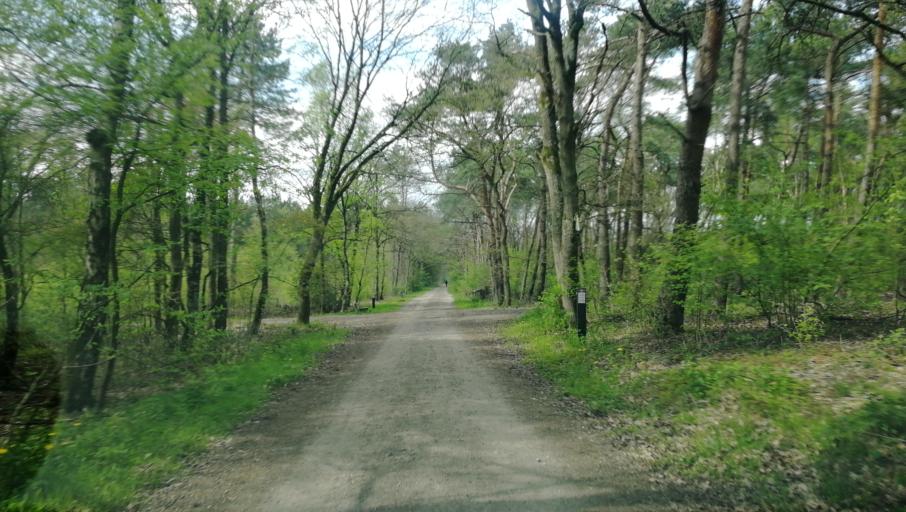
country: NL
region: Limburg
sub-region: Gemeente Peel en Maas
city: Maasbree
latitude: 51.3994
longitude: 5.9885
